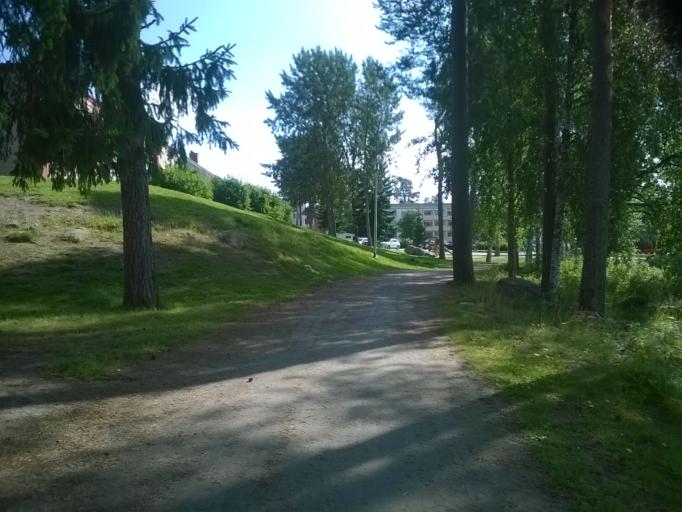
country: FI
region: Kainuu
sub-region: Kehys-Kainuu
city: Kuhmo
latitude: 64.1299
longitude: 29.5158
